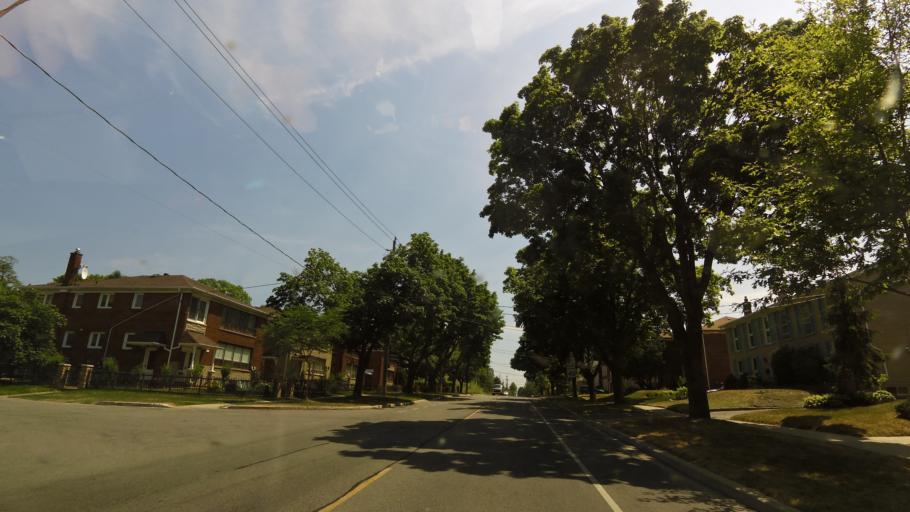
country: CA
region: Ontario
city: Etobicoke
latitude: 43.6367
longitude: -79.4869
